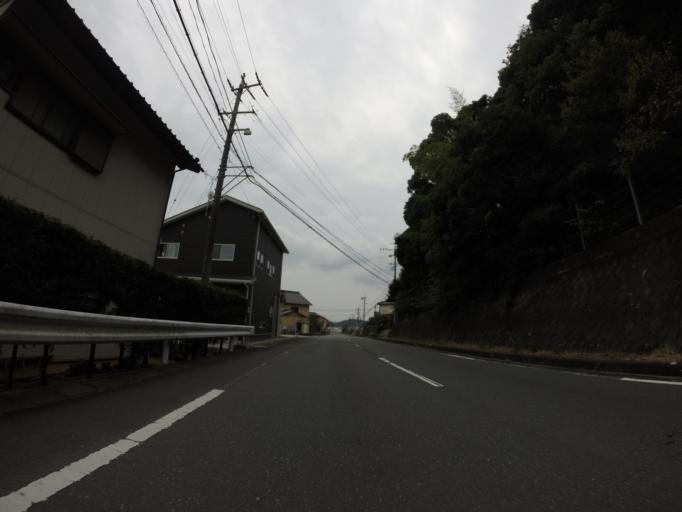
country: JP
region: Shizuoka
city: Kakegawa
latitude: 34.8137
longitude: 138.0161
